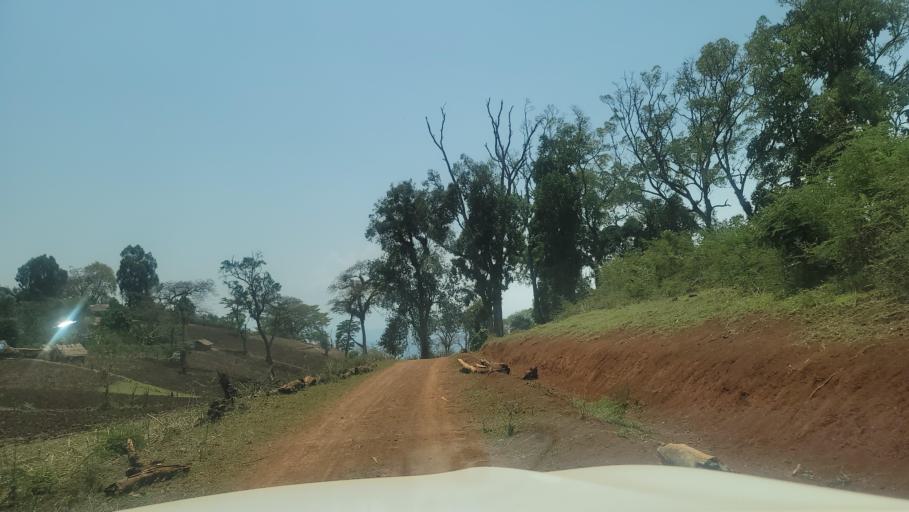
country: ET
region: Southern Nations, Nationalities, and People's Region
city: Bonga
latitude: 7.5328
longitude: 36.1888
